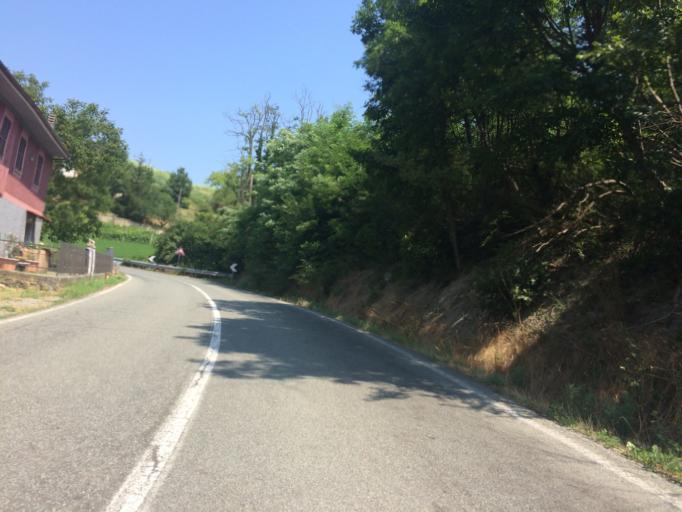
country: IT
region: Piedmont
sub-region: Provincia di Alessandria
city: Cartosio
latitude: 44.6119
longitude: 8.4167
